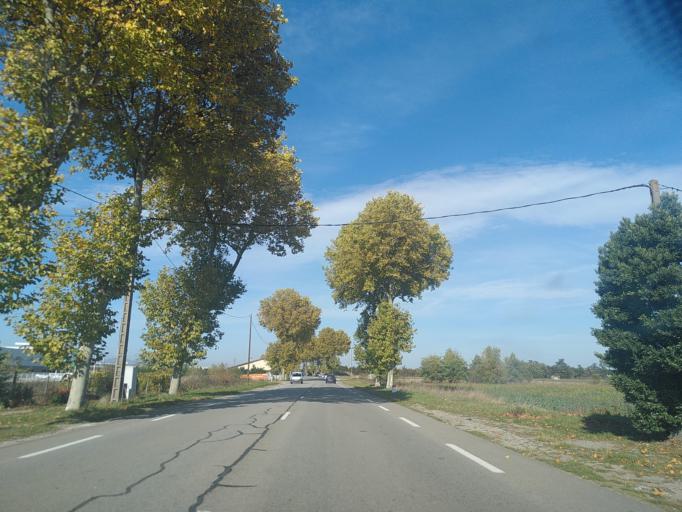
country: FR
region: Rhone-Alpes
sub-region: Departement de la Drome
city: Andancette
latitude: 45.2709
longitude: 4.8237
